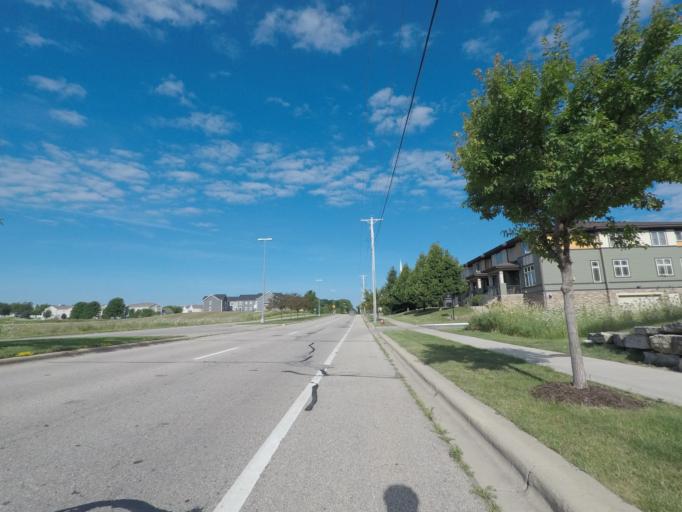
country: US
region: Wisconsin
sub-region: Dane County
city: Middleton
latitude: 43.0749
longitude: -89.5460
